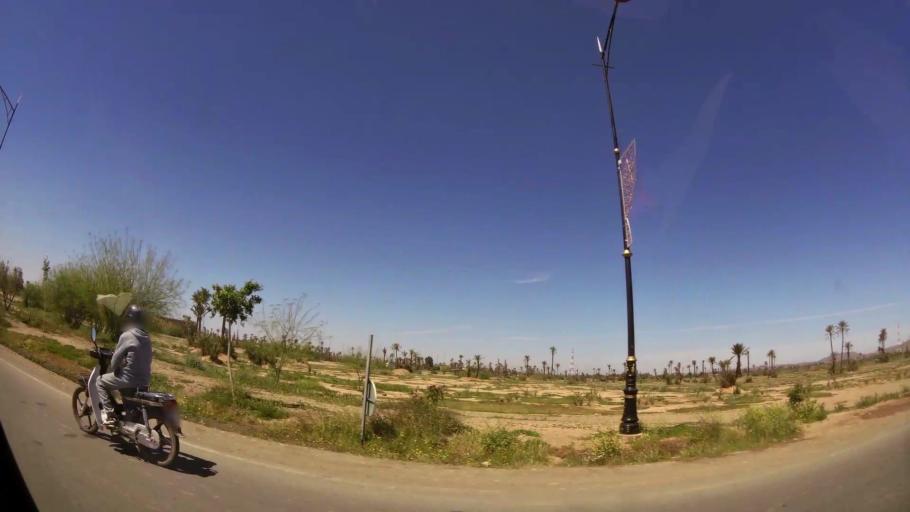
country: MA
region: Marrakech-Tensift-Al Haouz
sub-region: Marrakech
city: Marrakesh
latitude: 31.6878
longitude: -7.9925
